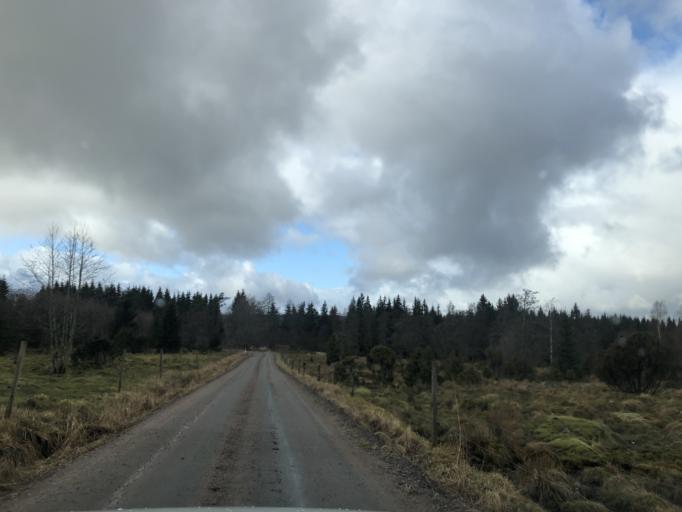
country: SE
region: Vaestra Goetaland
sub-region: Ulricehamns Kommun
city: Ulricehamn
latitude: 57.8284
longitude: 13.2469
